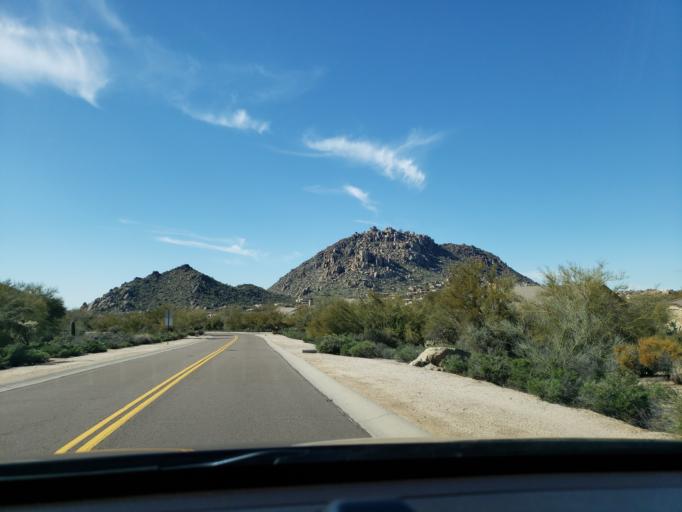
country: US
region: Arizona
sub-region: Maricopa County
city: Fountain Hills
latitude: 33.7048
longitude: -111.8263
